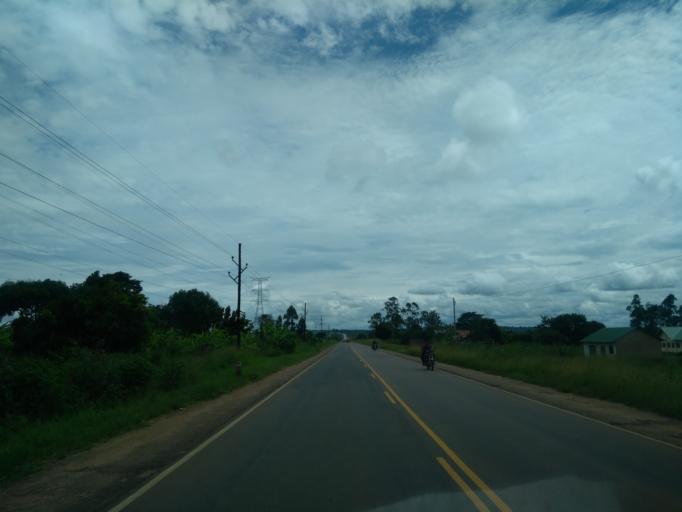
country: UG
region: Central Region
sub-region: Butambala District
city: Gombe
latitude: -0.0218
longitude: 32.0244
